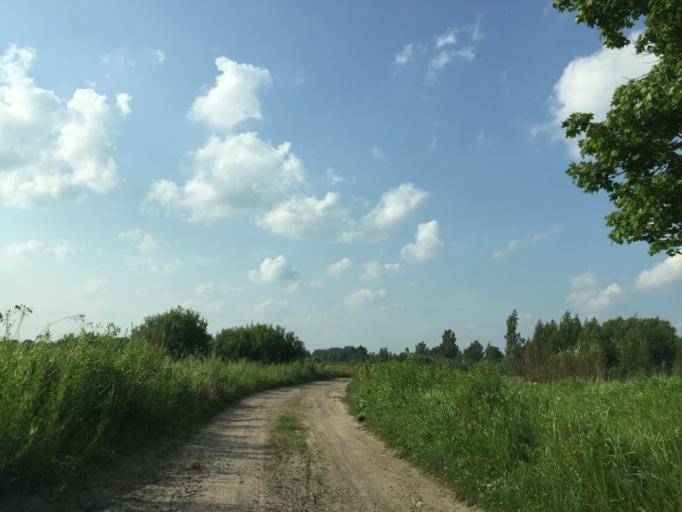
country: LV
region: Jelgava
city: Jelgava
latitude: 56.6722
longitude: 23.7108
